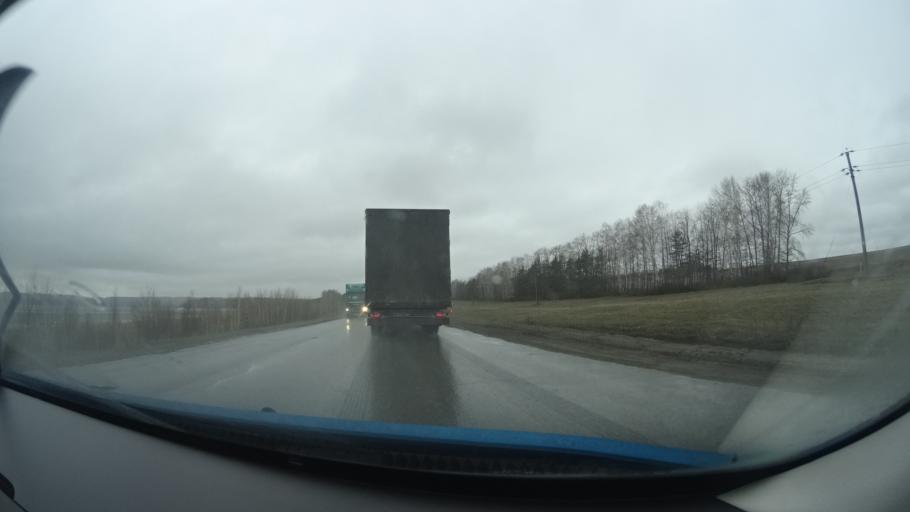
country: RU
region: Bashkortostan
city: Kandry
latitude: 54.5184
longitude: 54.0513
